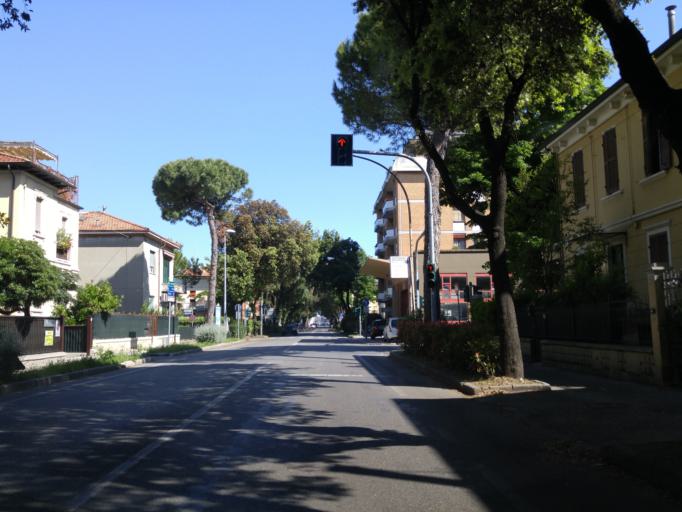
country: IT
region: The Marches
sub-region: Provincia di Pesaro e Urbino
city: Pesaro
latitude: 43.9104
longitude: 12.9181
